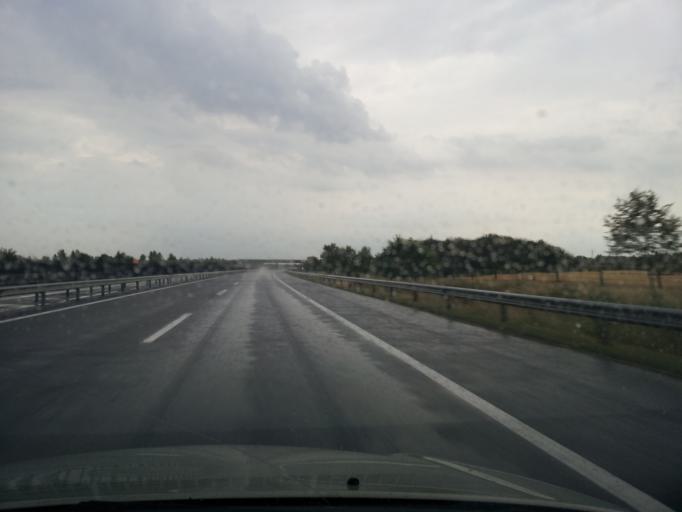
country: HU
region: Borsod-Abauj-Zemplen
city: Onod
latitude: 47.9761
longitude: 20.8979
